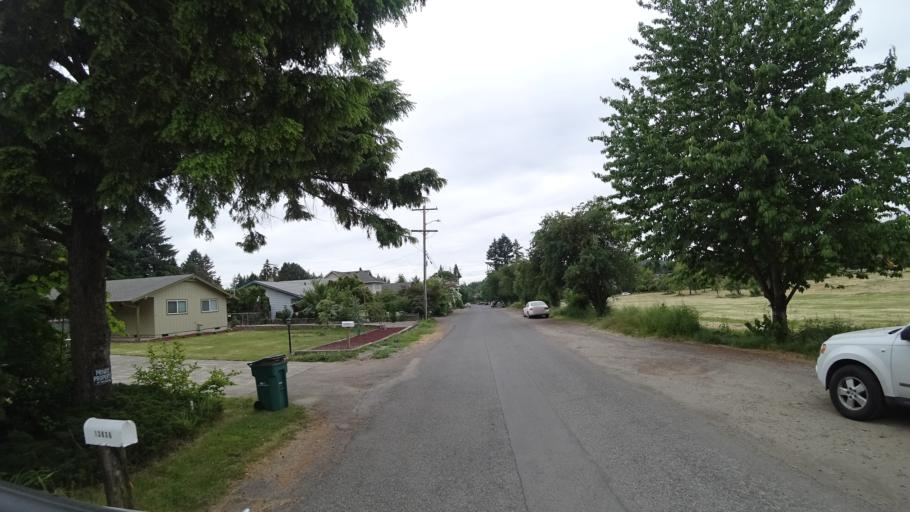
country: US
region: Oregon
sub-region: Clackamas County
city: Happy Valley
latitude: 45.4887
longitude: -122.5210
